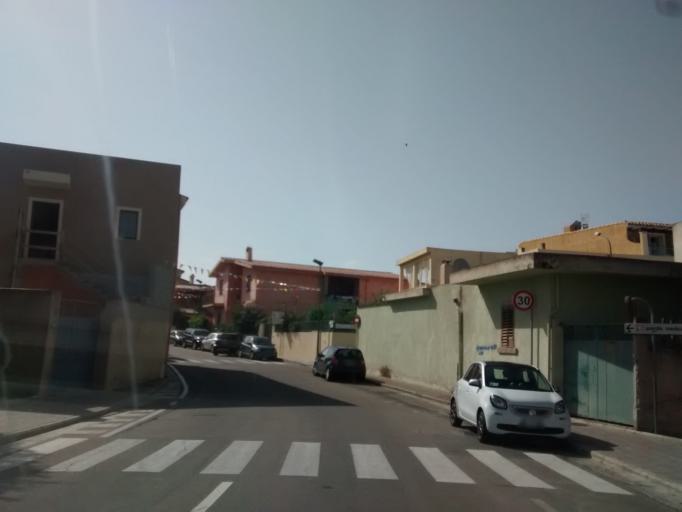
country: IT
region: Sardinia
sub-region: Provincia di Cagliari
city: Villasimius
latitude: 39.1461
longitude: 9.5191
